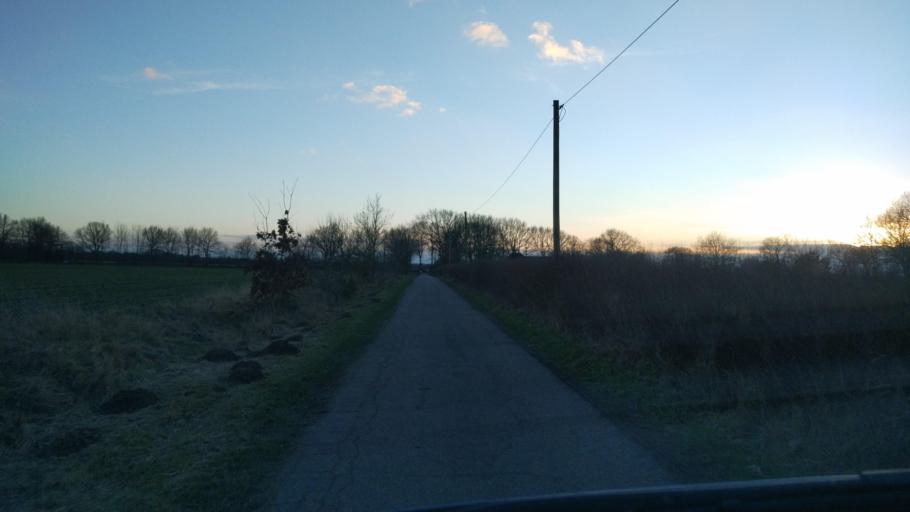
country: DE
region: Schleswig-Holstein
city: Gross Rheide
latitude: 54.4441
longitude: 9.4111
